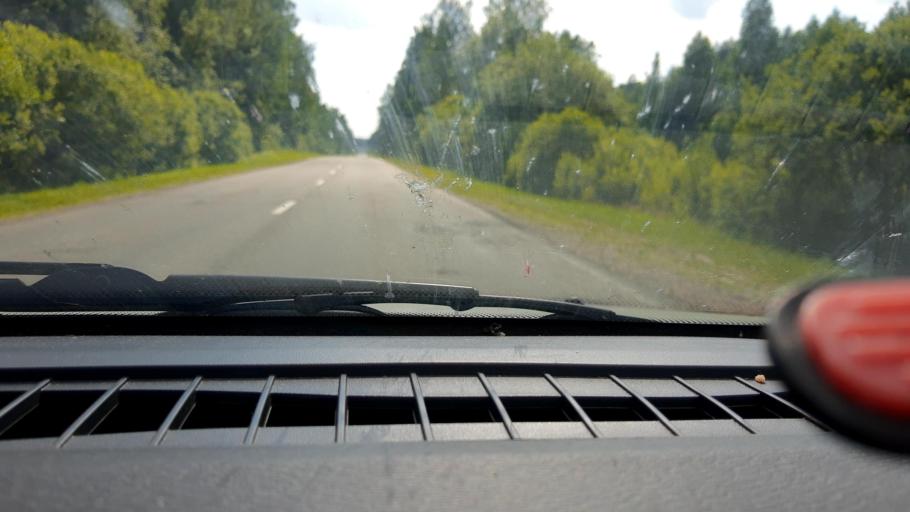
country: RU
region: Nizjnij Novgorod
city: Uren'
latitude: 57.3022
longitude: 45.6673
